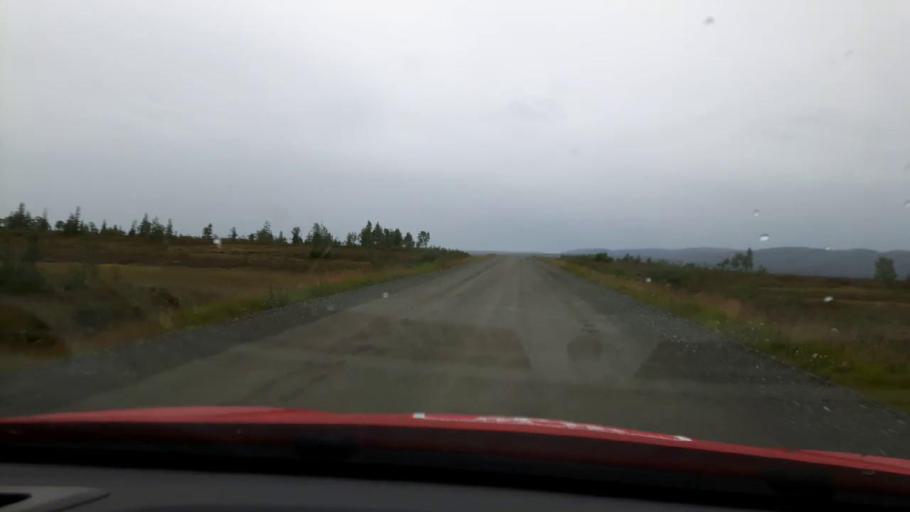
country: NO
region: Nord-Trondelag
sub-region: Meraker
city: Meraker
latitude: 63.5901
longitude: 12.2692
